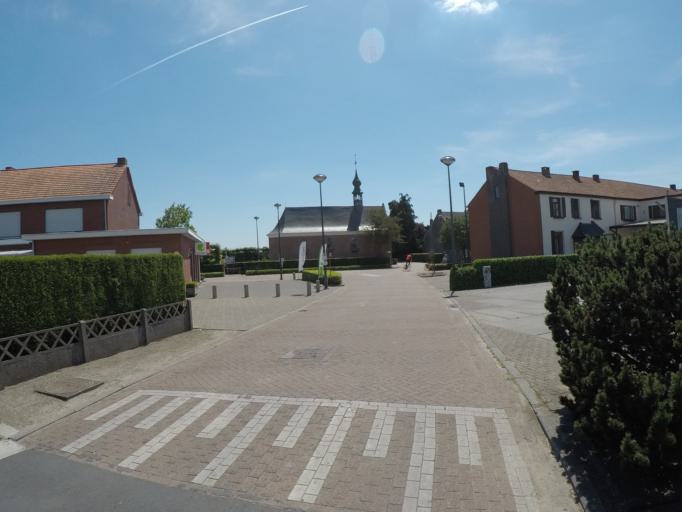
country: BE
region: Flanders
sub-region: Provincie Antwerpen
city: Wuustwezel
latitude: 51.3800
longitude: 4.5606
